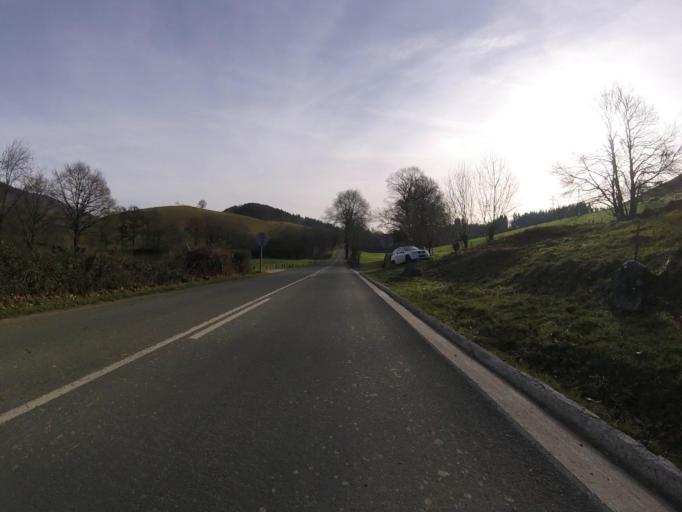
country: ES
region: Navarre
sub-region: Provincia de Navarra
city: Areso
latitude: 43.1059
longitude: -1.9616
